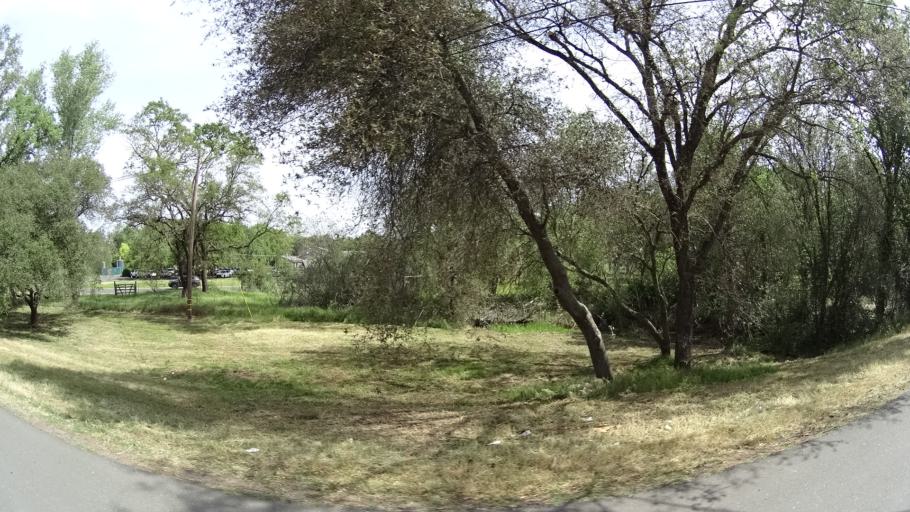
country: US
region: California
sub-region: Placer County
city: Loomis
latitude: 38.8138
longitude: -121.2076
